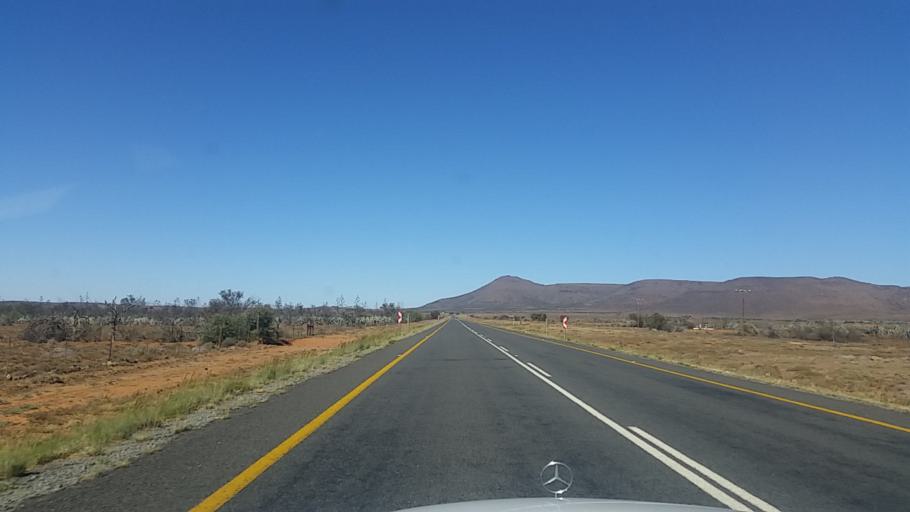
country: ZA
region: Eastern Cape
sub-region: Cacadu District Municipality
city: Graaff-Reinet
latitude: -32.0110
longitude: 24.6521
